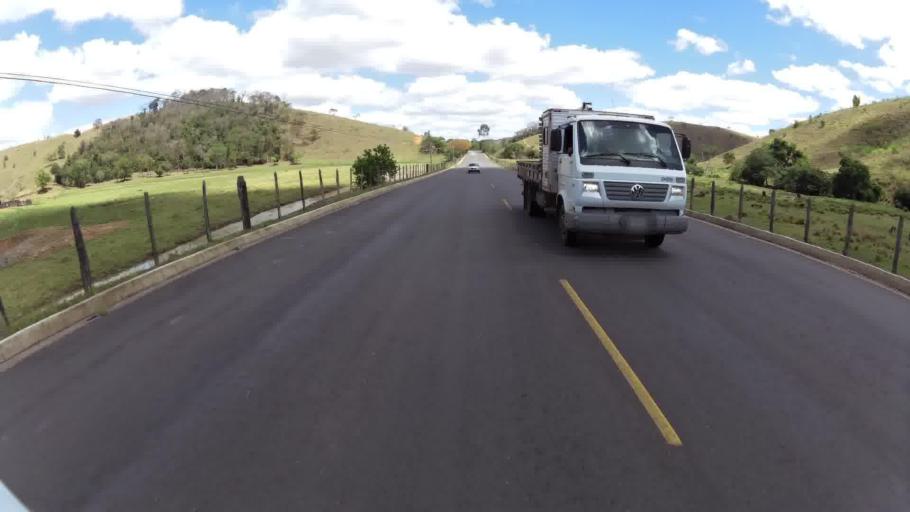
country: BR
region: Rio de Janeiro
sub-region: Cambuci
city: Cambuci
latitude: -21.3927
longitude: -41.9717
